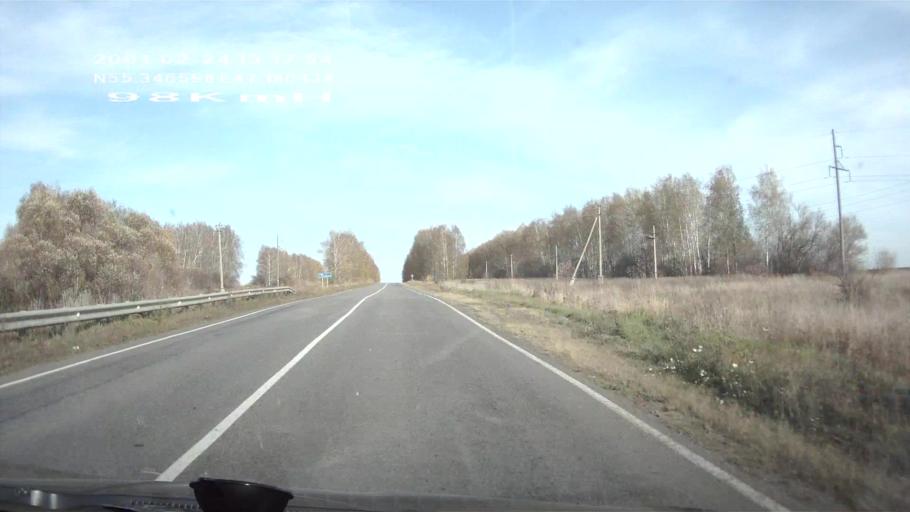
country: RU
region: Chuvashia
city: Ibresi
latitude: 55.3465
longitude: 47.1803
